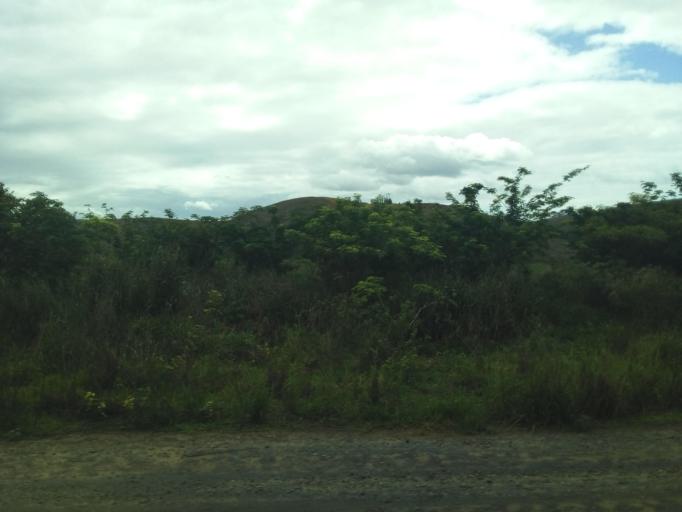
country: BR
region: Minas Gerais
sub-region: Governador Valadares
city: Governador Valadares
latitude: -19.0854
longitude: -42.1620
